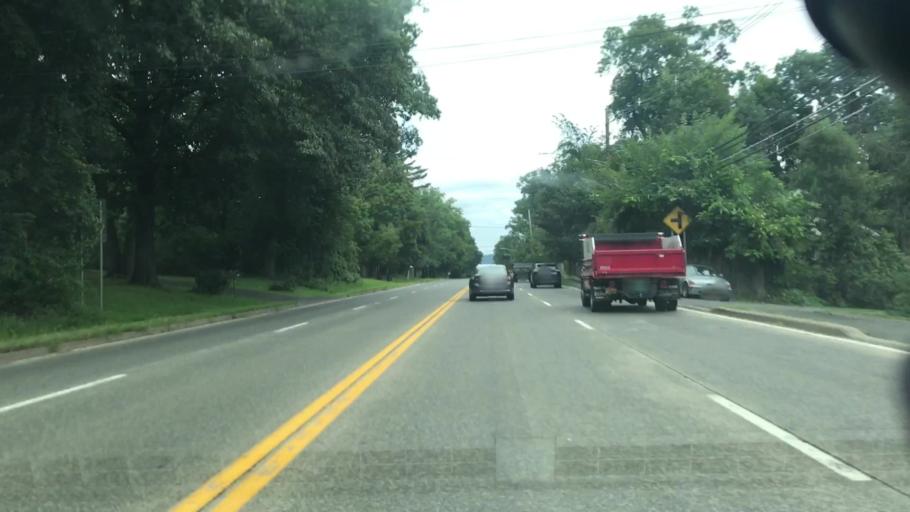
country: US
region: New York
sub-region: Rockland County
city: Bardonia
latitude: 41.1233
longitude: -73.9925
